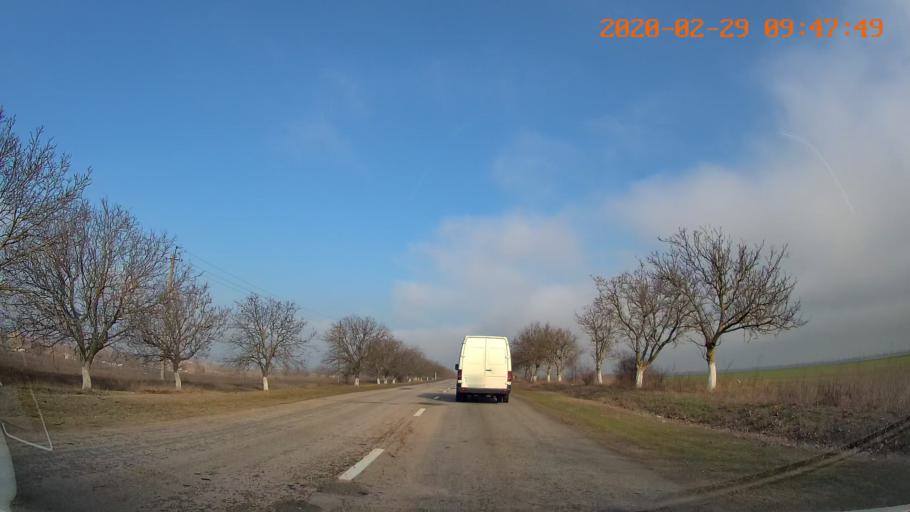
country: MD
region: Telenesti
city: Crasnoe
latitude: 46.6808
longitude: 29.7879
